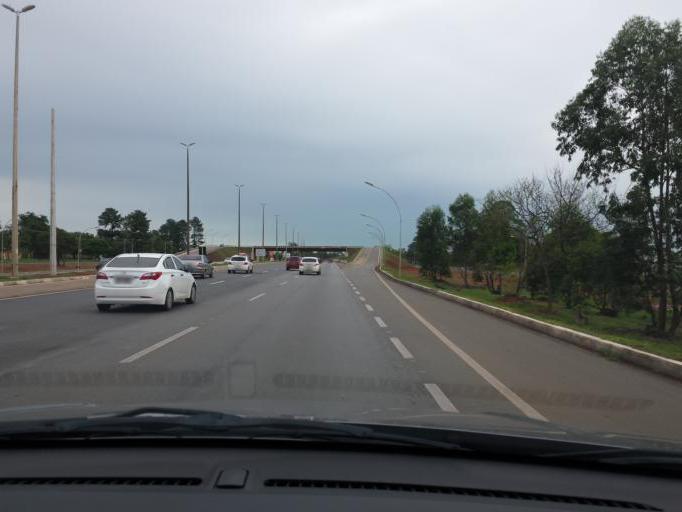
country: BR
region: Federal District
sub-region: Brasilia
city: Brasilia
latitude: -15.9096
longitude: -47.9664
